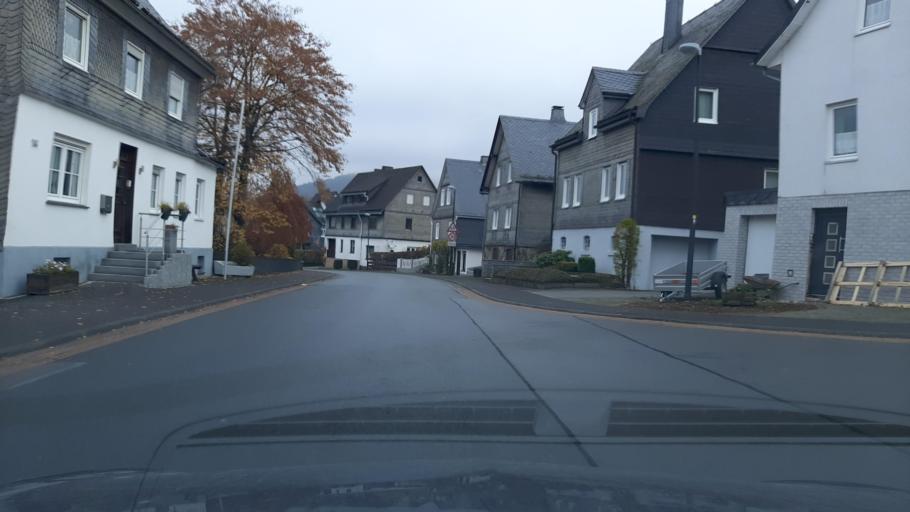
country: DE
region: North Rhine-Westphalia
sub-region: Regierungsbezirk Arnsberg
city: Winterberg
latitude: 51.2501
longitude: 8.4715
